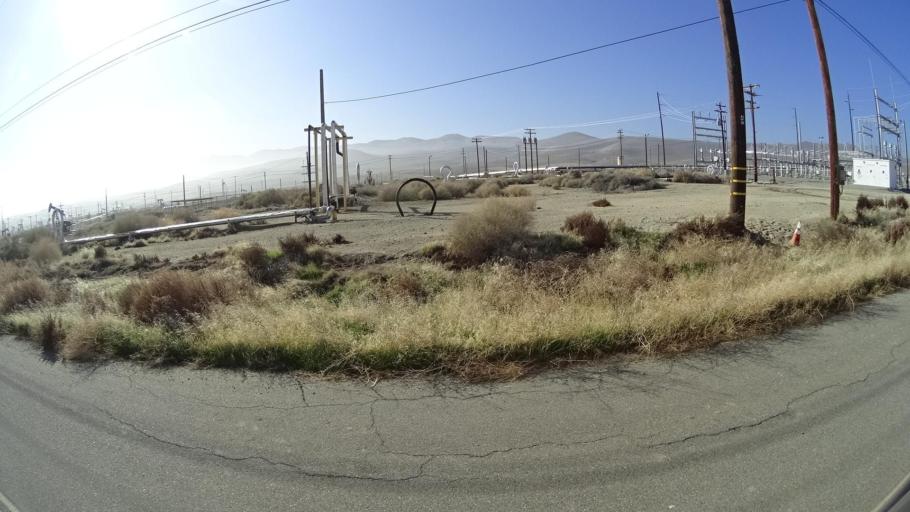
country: US
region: California
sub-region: Kern County
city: Taft Heights
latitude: 35.2259
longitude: -119.6266
